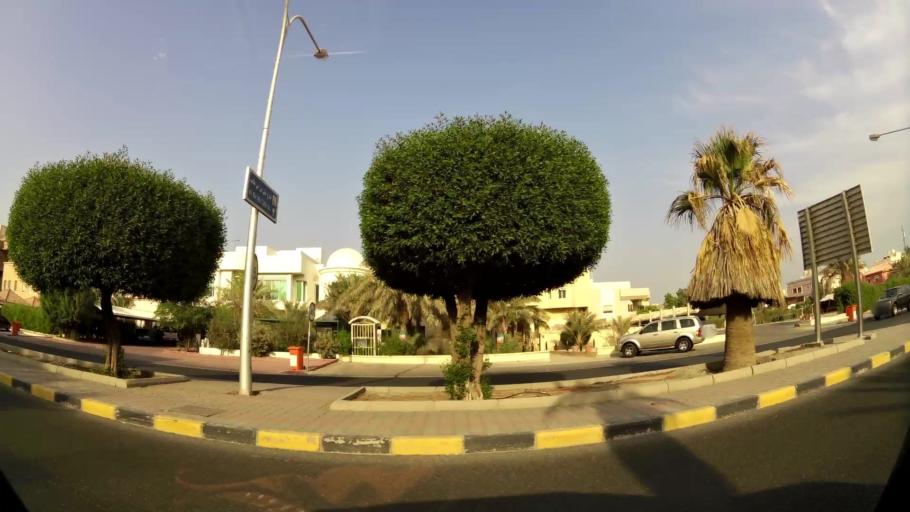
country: KW
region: Muhafazat Hawalli
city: Hawalli
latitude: 29.3157
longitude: 48.0095
